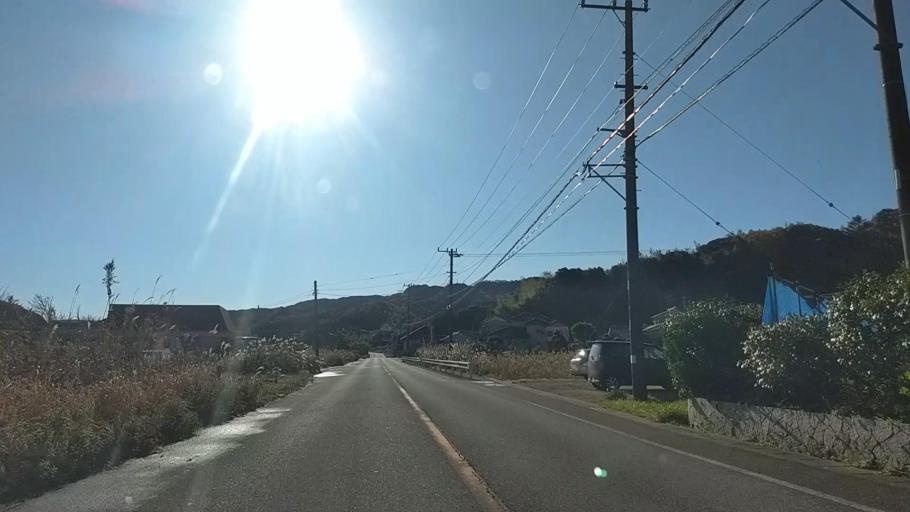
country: JP
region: Chiba
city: Futtsu
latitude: 35.2740
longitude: 139.8626
